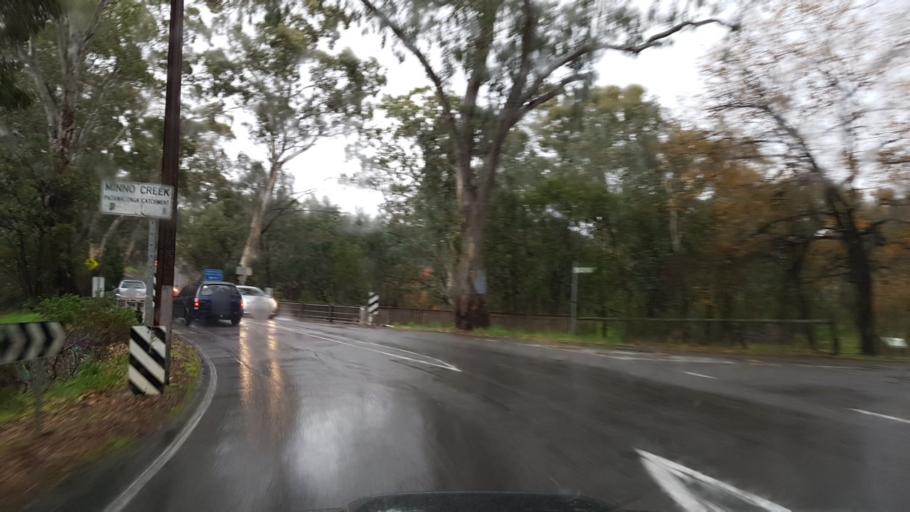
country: AU
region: South Australia
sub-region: Mitcham
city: Blackwood
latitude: -35.0293
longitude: 138.6256
